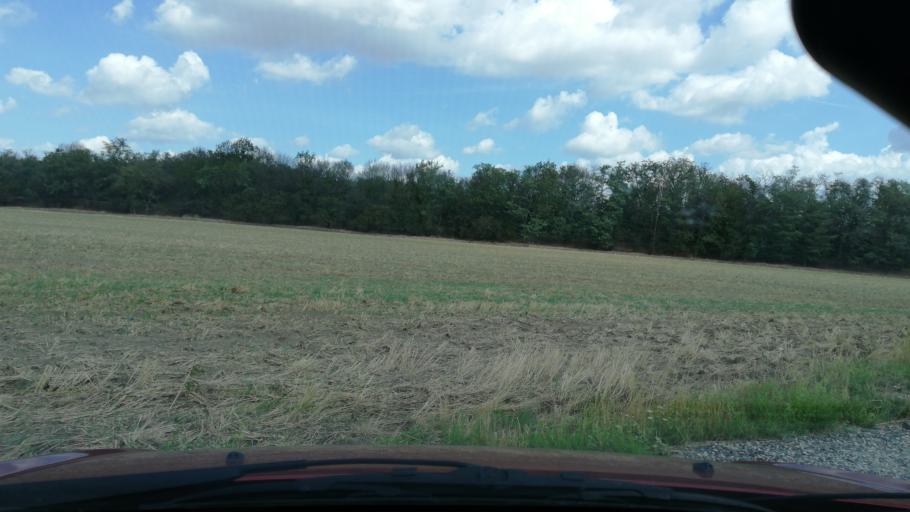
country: DE
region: Saxony-Anhalt
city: Landsberg
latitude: 51.5232
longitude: 12.1415
